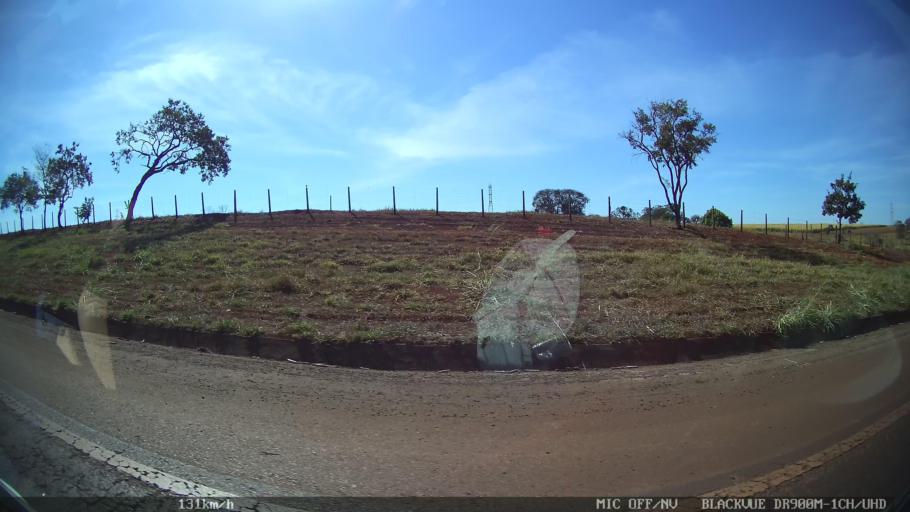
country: BR
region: Sao Paulo
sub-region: Ipua
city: Ipua
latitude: -20.4533
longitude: -48.1673
